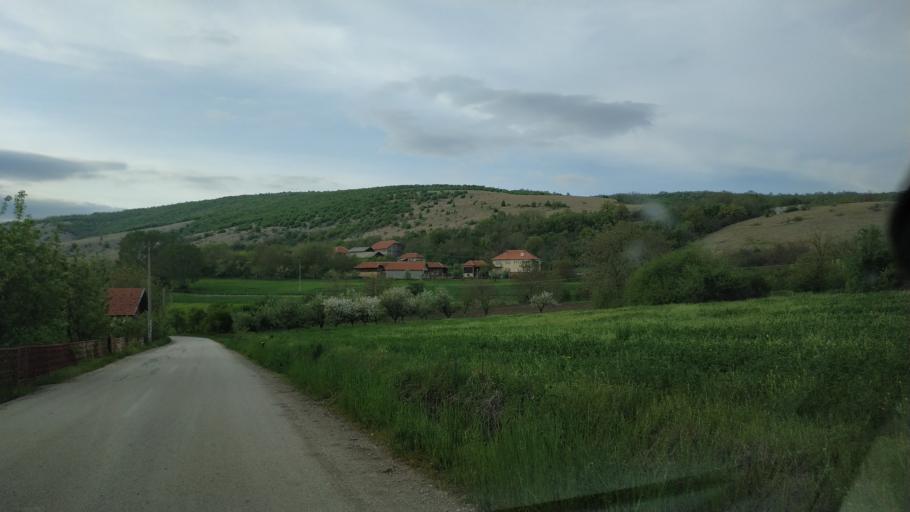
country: RS
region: Central Serbia
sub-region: Zajecarski Okrug
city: Soko Banja
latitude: 43.5244
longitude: 21.8608
